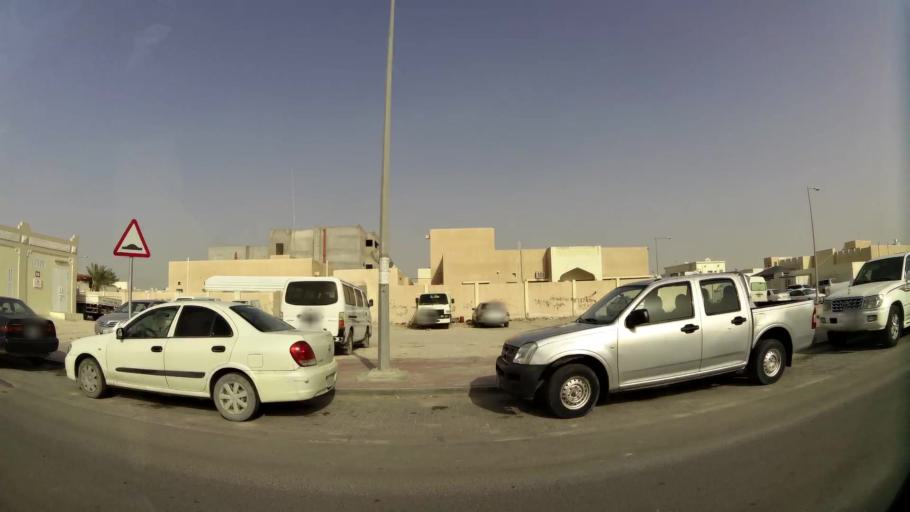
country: QA
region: Baladiyat ar Rayyan
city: Ar Rayyan
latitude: 25.2378
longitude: 51.4368
